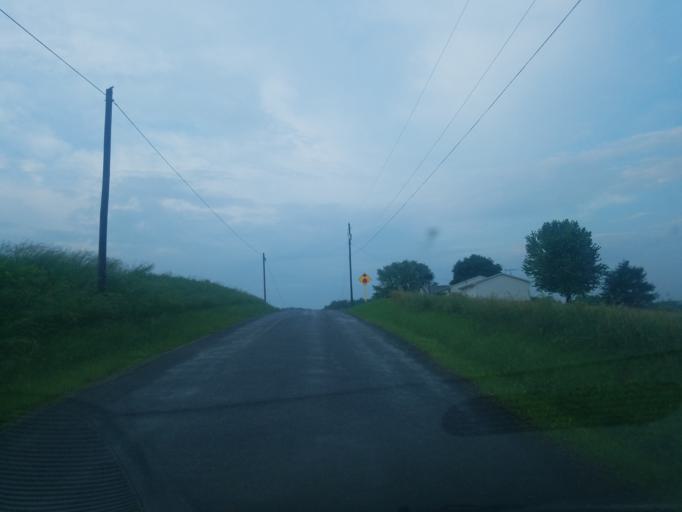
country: US
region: Ohio
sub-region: Columbiana County
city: Salem
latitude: 40.7798
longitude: -80.9556
